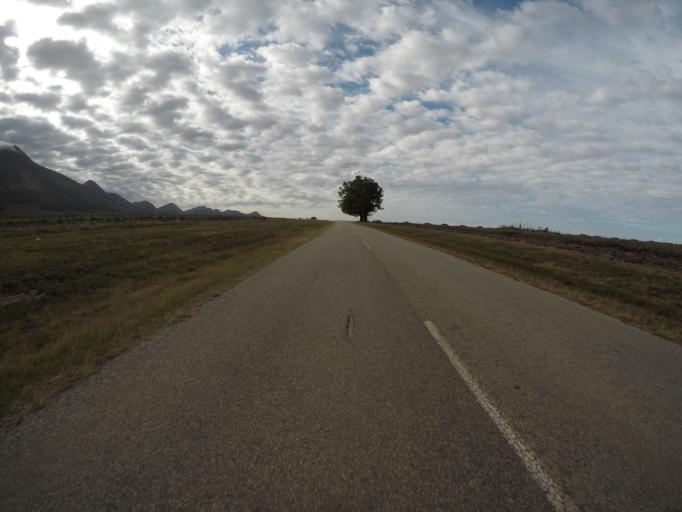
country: ZA
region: Eastern Cape
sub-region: Cacadu District Municipality
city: Kareedouw
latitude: -34.0409
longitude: 24.4084
